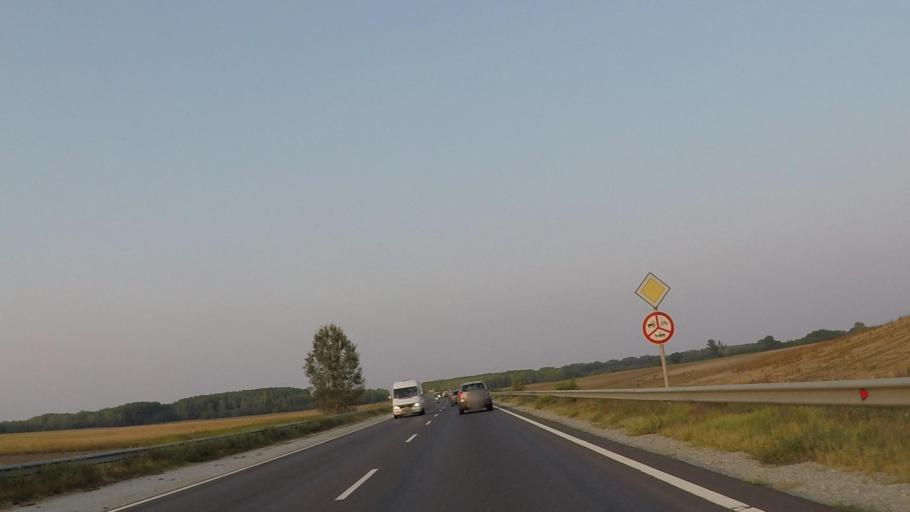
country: HU
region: Pest
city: Abony
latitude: 47.2008
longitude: 19.9504
